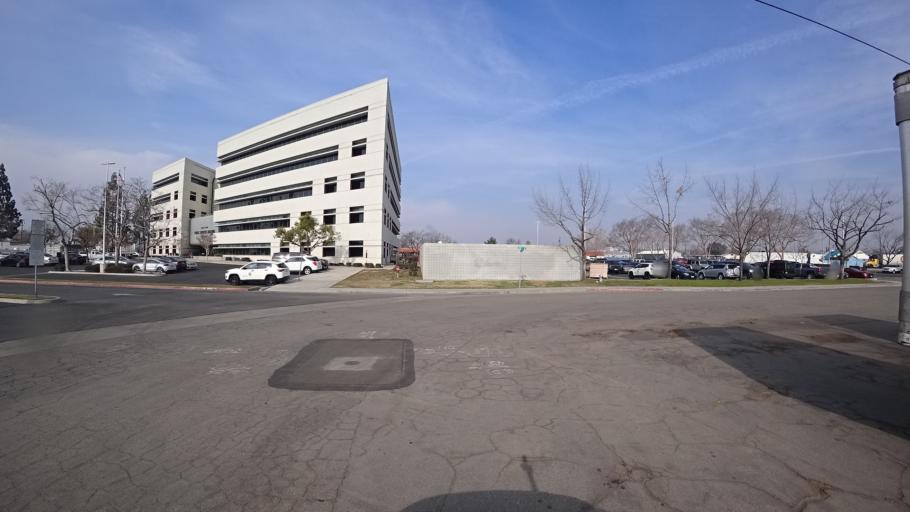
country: US
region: California
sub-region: Kern County
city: Bakersfield
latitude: 35.3828
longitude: -119.0141
